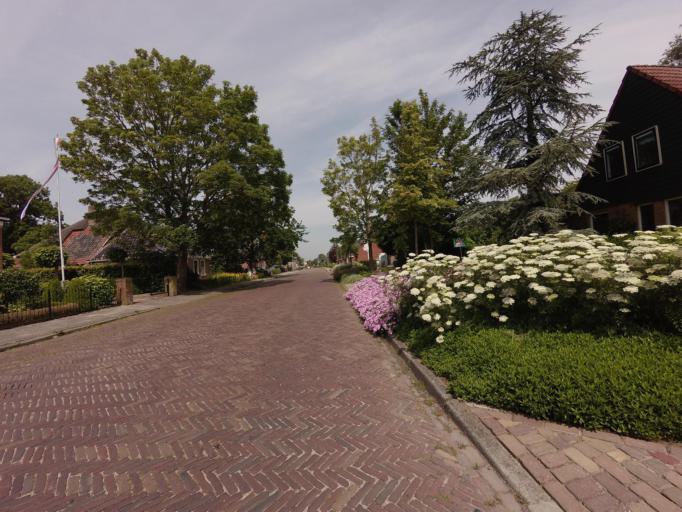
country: NL
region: North Holland
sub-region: Gemeente Hoorn
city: Hoorn
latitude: 52.6848
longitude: 5.0214
